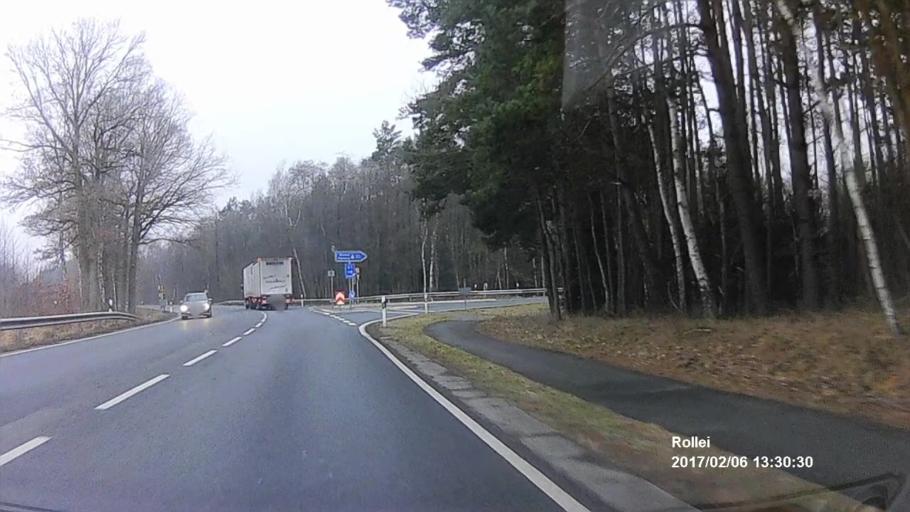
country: DE
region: Lower Saxony
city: Walsrode
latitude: 52.8391
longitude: 9.5946
